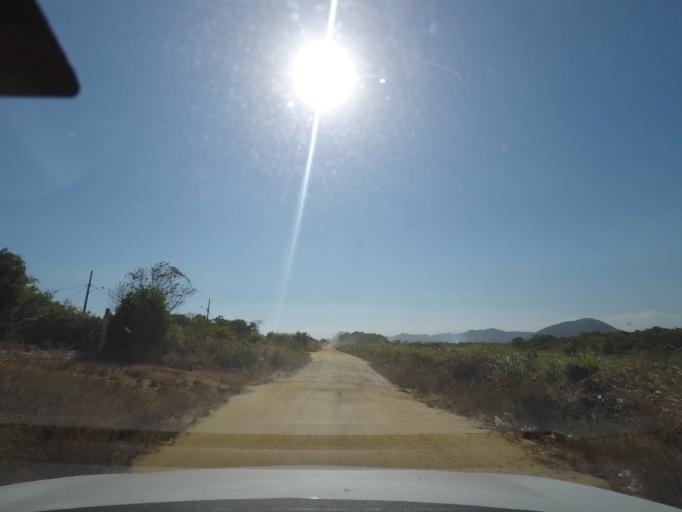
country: BR
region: Rio de Janeiro
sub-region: Marica
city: Marica
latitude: -22.9650
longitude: -42.9113
